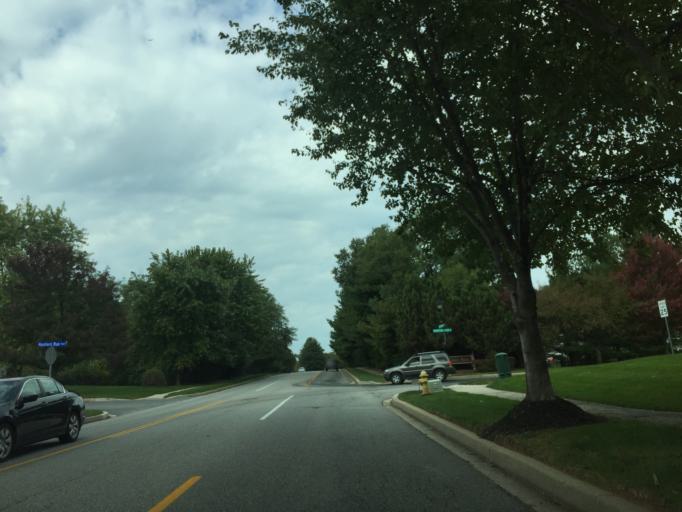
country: US
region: Maryland
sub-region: Harford County
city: Bel Air South
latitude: 39.4971
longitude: -76.3197
